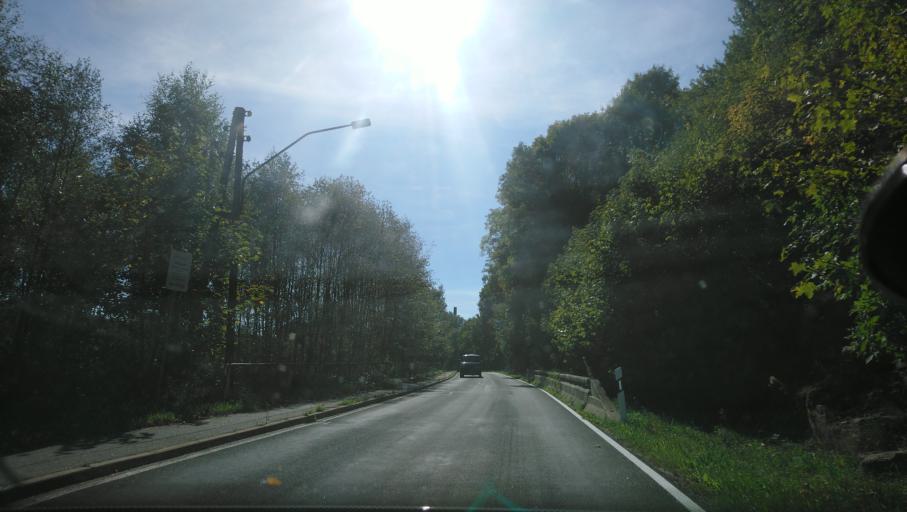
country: DE
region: Saxony
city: Barenstein
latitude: 50.5071
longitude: 13.0296
